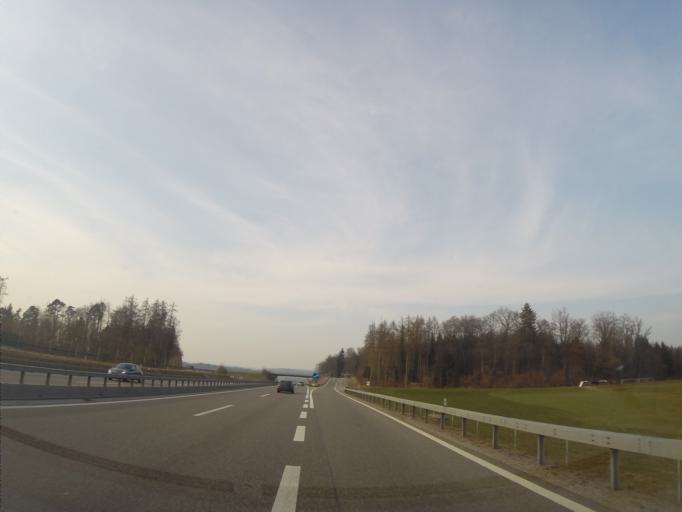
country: CH
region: Zurich
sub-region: Bezirk Andelfingen
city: Kleinandelfingen
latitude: 47.6142
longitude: 8.6857
